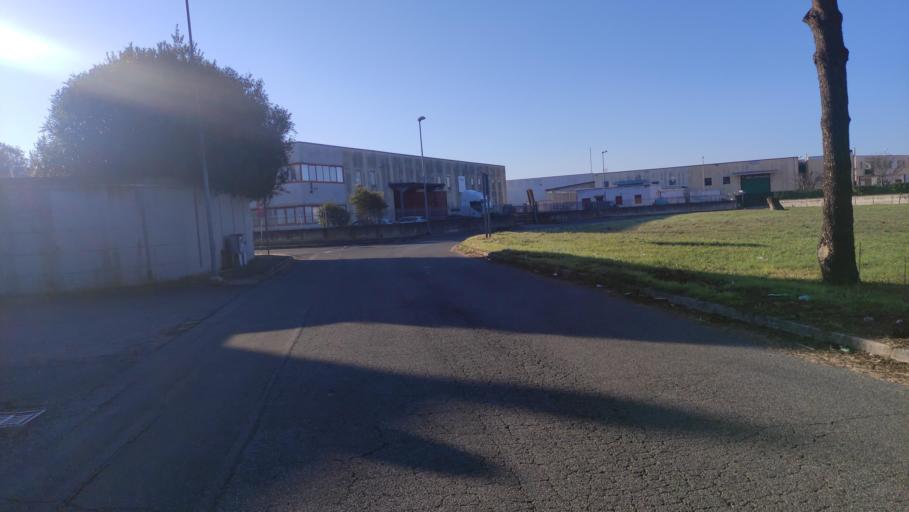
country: IT
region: Latium
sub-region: Citta metropolitana di Roma Capitale
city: Fiano Romano
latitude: 42.1378
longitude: 12.5862
